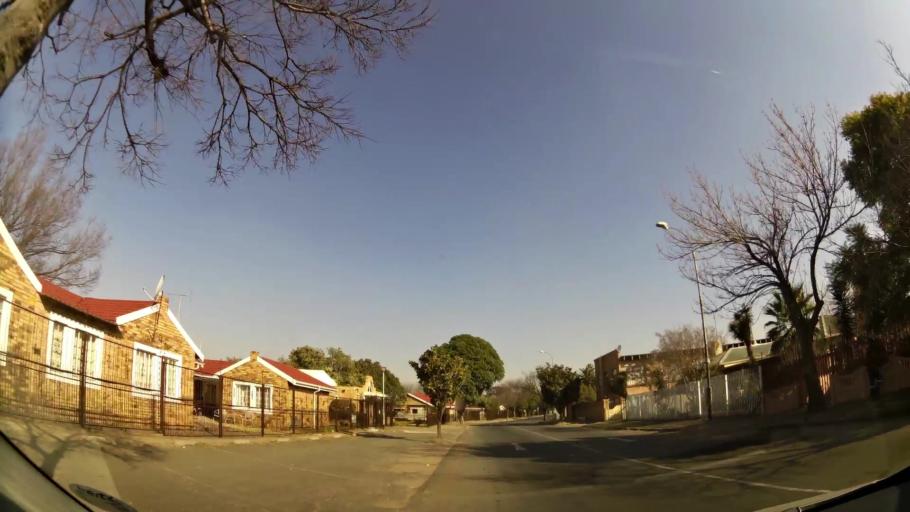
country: ZA
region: Gauteng
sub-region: West Rand District Municipality
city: Randfontein
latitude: -26.1758
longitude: 27.7076
